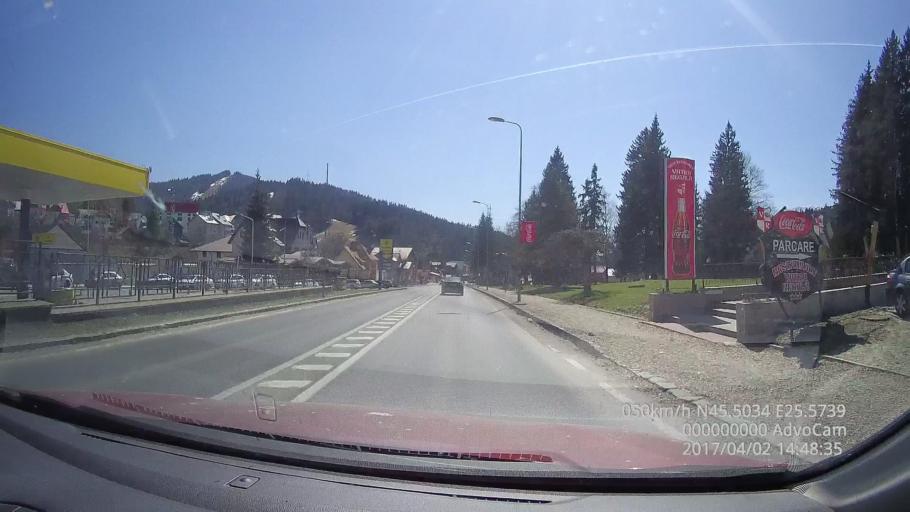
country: RO
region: Brasov
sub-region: Oras Predeal
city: Predeal
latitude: 45.5031
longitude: 25.5740
